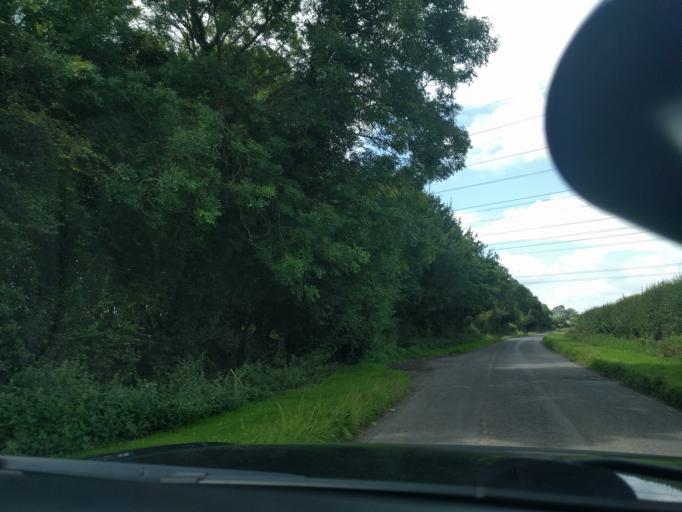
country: GB
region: England
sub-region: Wiltshire
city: Melksham
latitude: 51.3976
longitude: -2.1471
